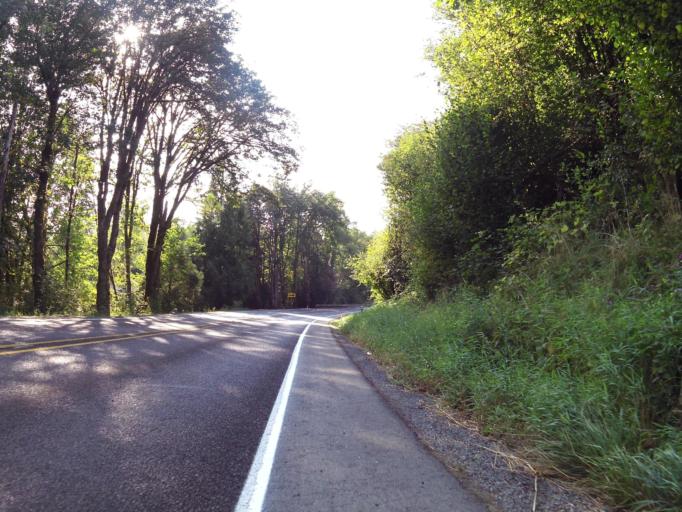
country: US
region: Washington
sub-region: Mason County
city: Belfair
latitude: 47.5110
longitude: -122.7906
